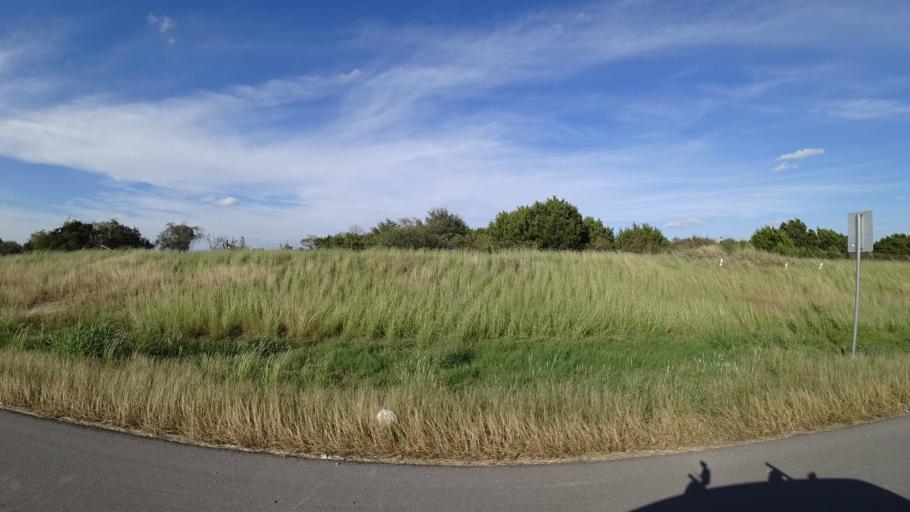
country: US
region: Texas
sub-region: Travis County
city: Wells Branch
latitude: 30.4609
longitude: -97.6962
